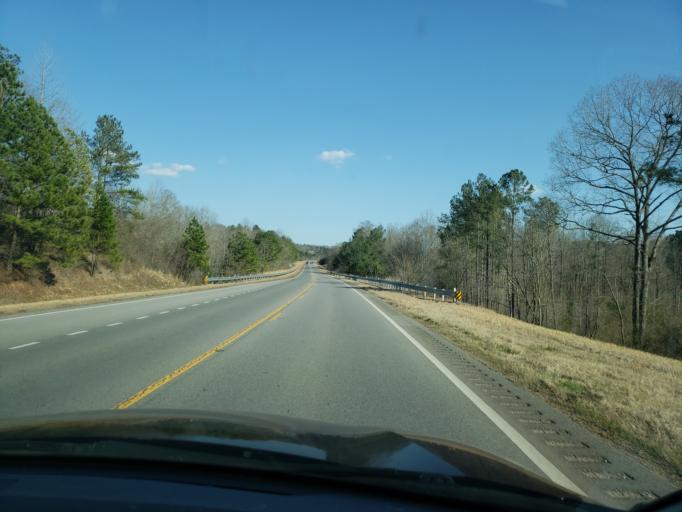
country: US
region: Alabama
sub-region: Cleburne County
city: Heflin
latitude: 33.5054
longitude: -85.6178
